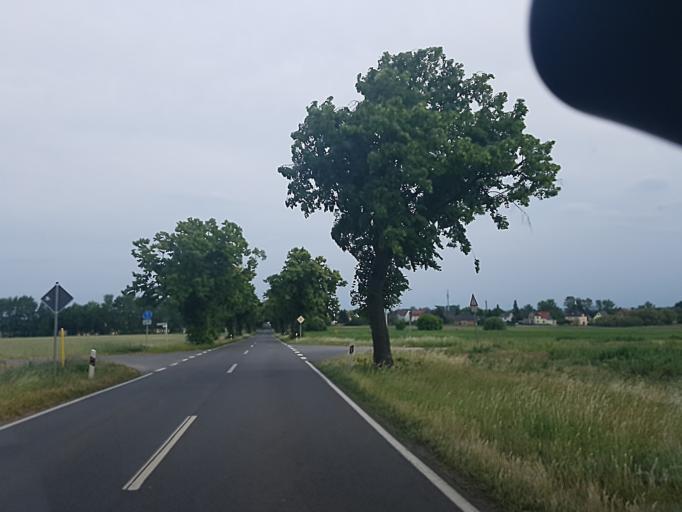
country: DE
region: Saxony-Anhalt
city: Wittenburg
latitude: 51.8840
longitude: 12.6278
